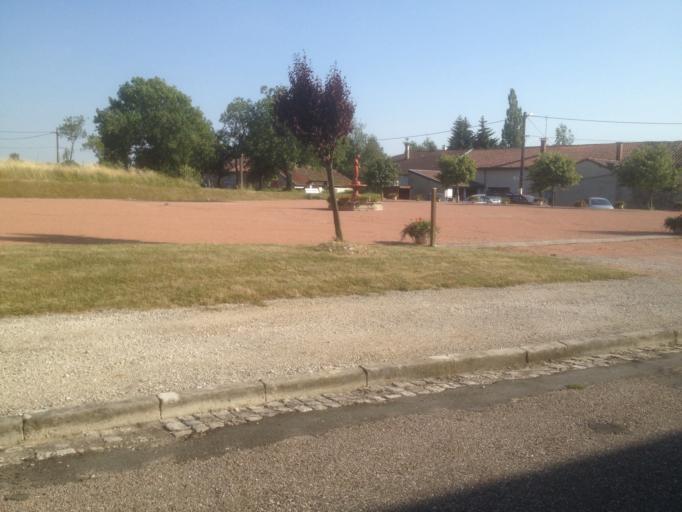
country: FR
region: Champagne-Ardenne
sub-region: Departement de la Haute-Marne
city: Doulaincourt-Saucourt
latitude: 48.4421
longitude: 5.3365
